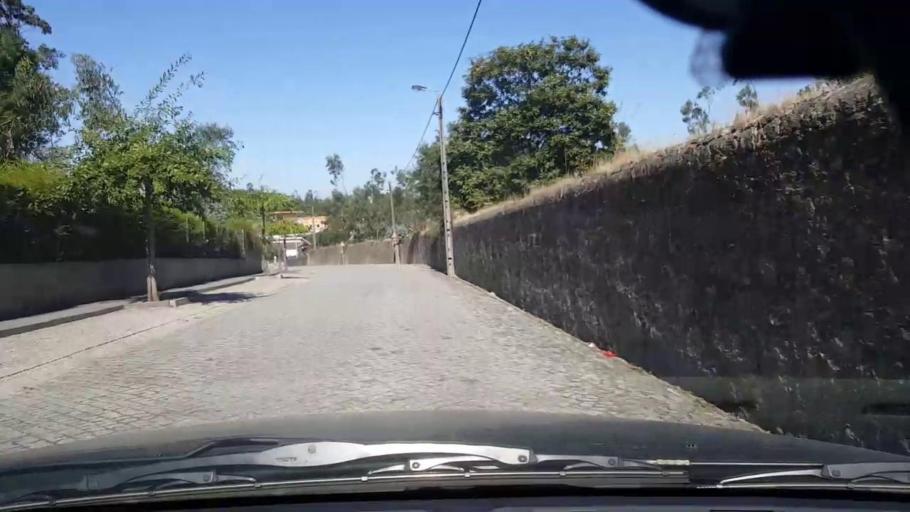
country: PT
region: Porto
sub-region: Maia
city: Gemunde
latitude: 41.3314
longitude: -8.6445
